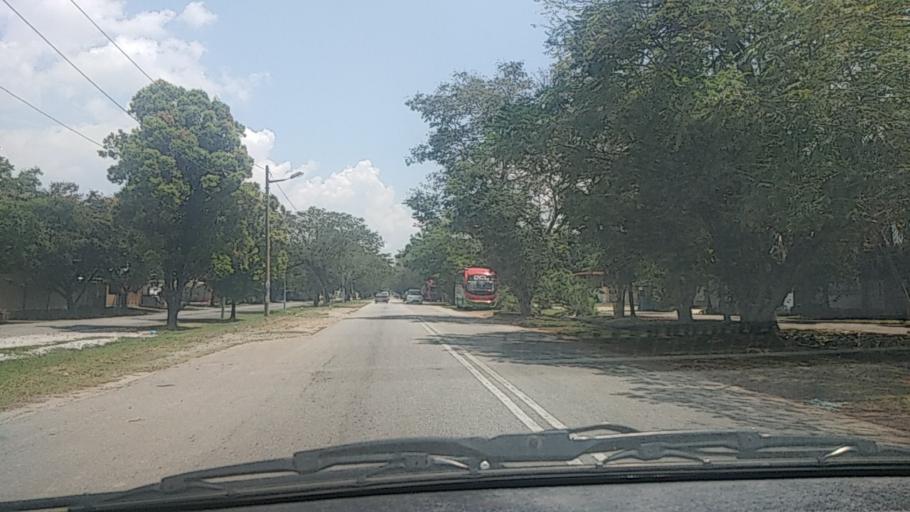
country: MY
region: Kedah
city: Sungai Petani
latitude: 5.6459
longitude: 100.5246
